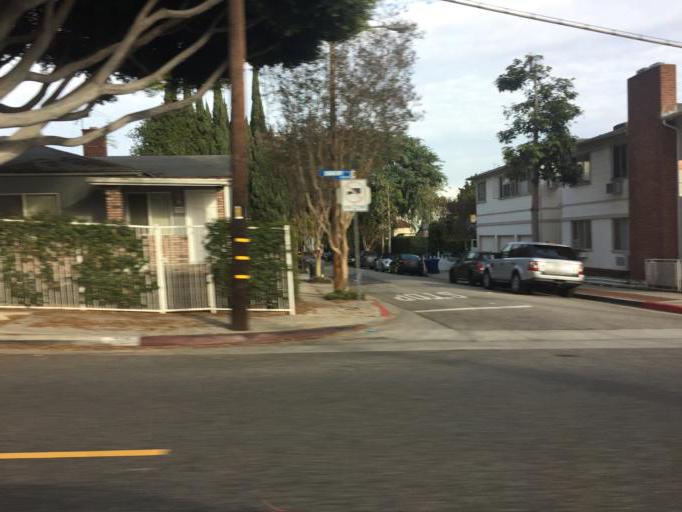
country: US
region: California
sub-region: Los Angeles County
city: Beverly Hills
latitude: 34.0844
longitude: -118.3898
